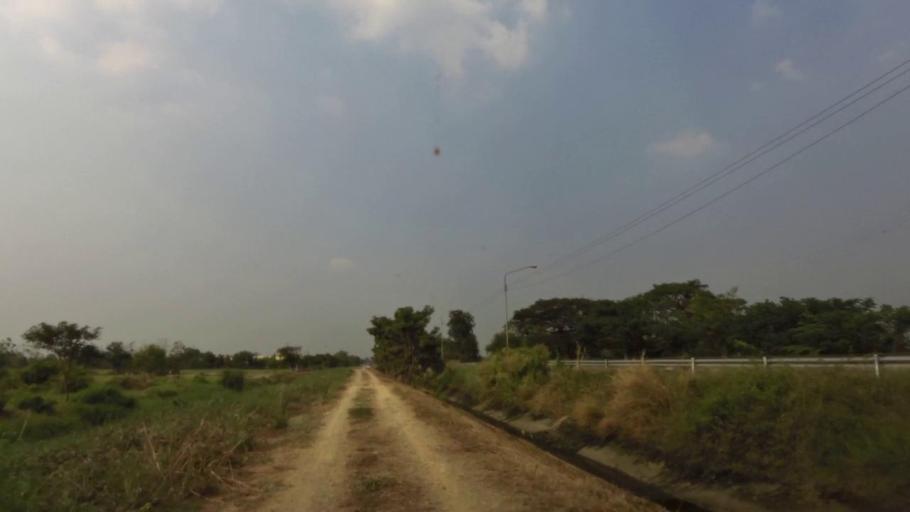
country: TH
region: Phra Nakhon Si Ayutthaya
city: Phra Nakhon Si Ayutthaya
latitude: 14.3141
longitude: 100.5614
